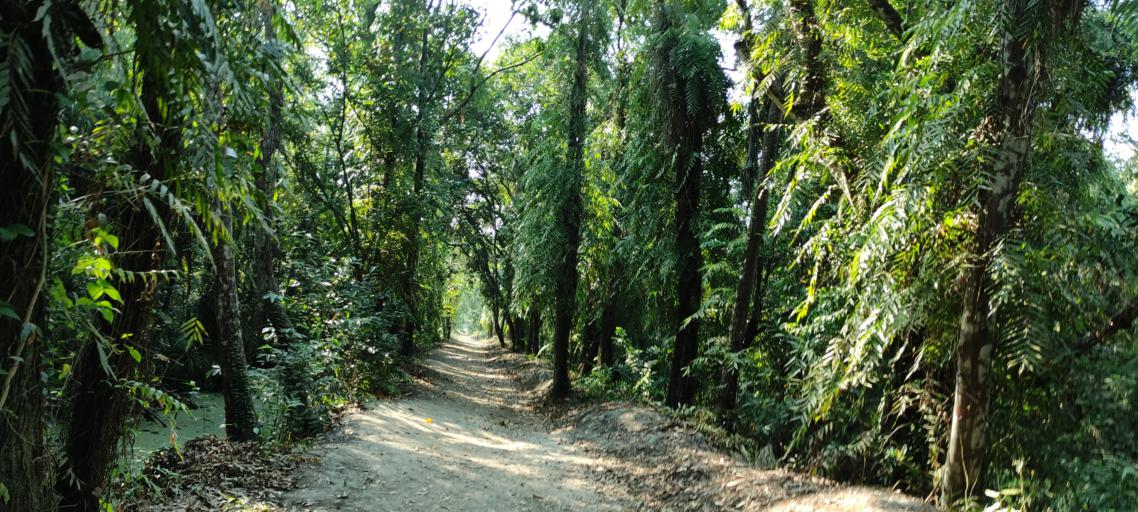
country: IN
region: Kerala
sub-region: Alappuzha
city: Shertallai
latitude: 9.6183
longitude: 76.3862
